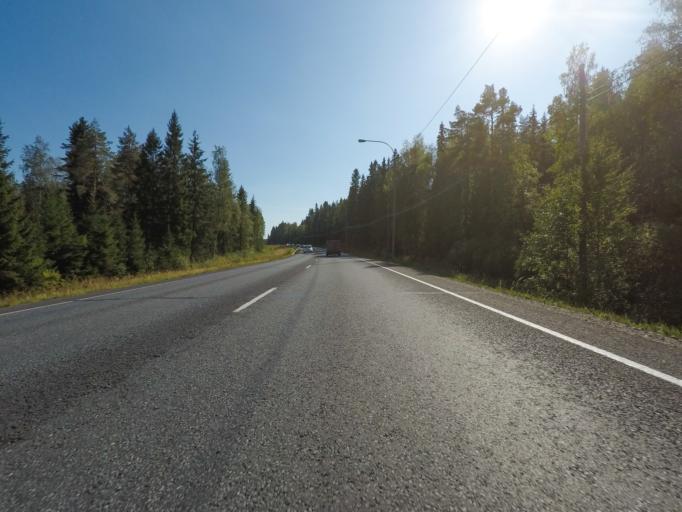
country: FI
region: Northern Savo
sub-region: Varkaus
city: Leppaevirta
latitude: 62.5571
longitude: 27.6195
